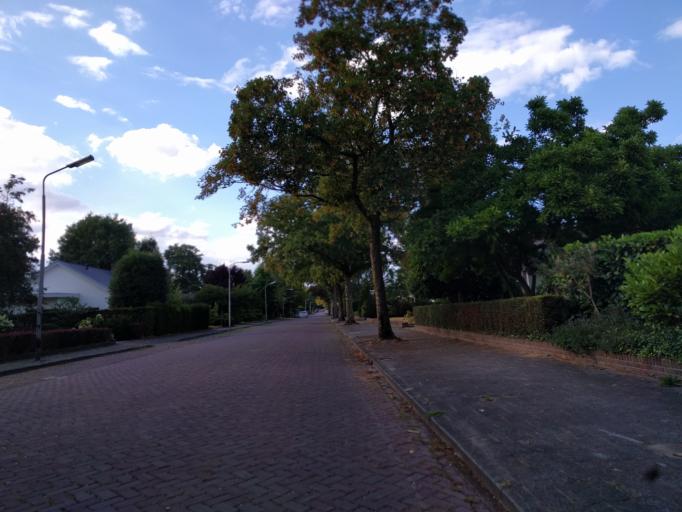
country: NL
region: Gelderland
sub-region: Gemeente Nijmegen
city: Nijmegen
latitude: 51.8211
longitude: 5.8769
